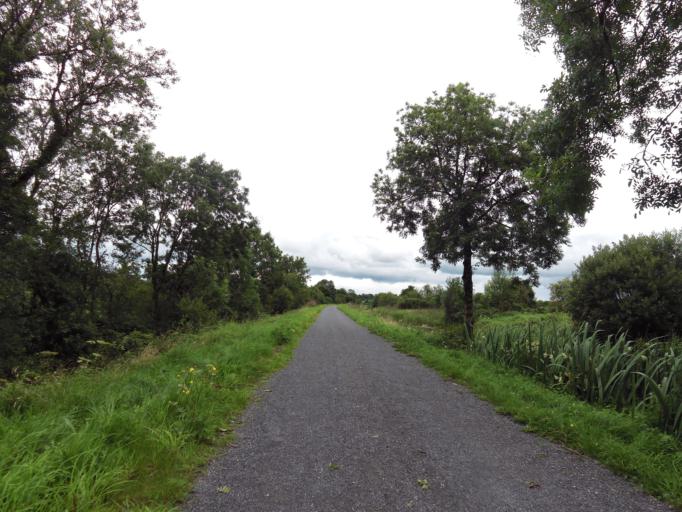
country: IE
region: Leinster
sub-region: An Iarmhi
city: An Muileann gCearr
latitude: 53.5103
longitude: -7.4228
